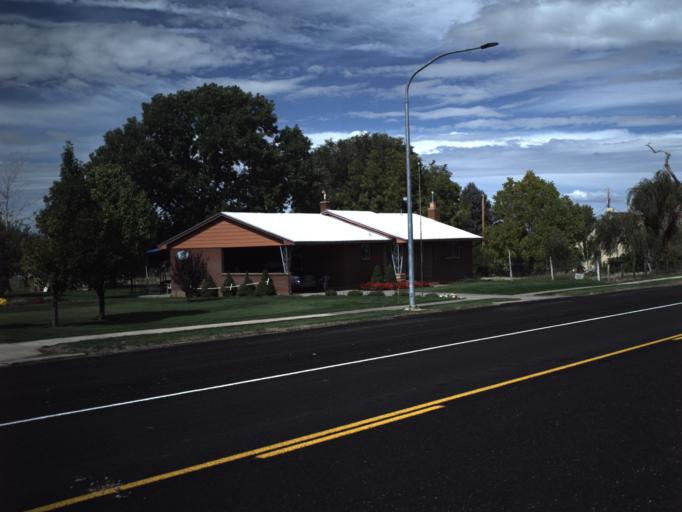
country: US
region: Utah
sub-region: Millard County
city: Fillmore
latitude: 38.7981
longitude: -112.4377
